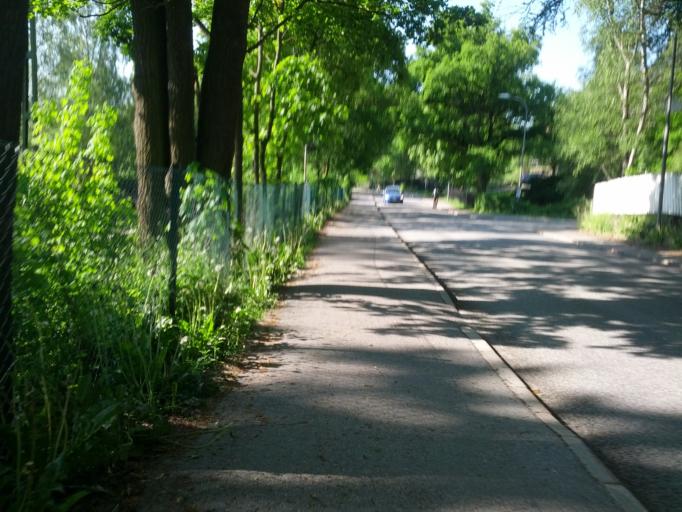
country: SE
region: Stockholm
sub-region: Danderyds Kommun
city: Djursholm
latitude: 59.4040
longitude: 18.0595
